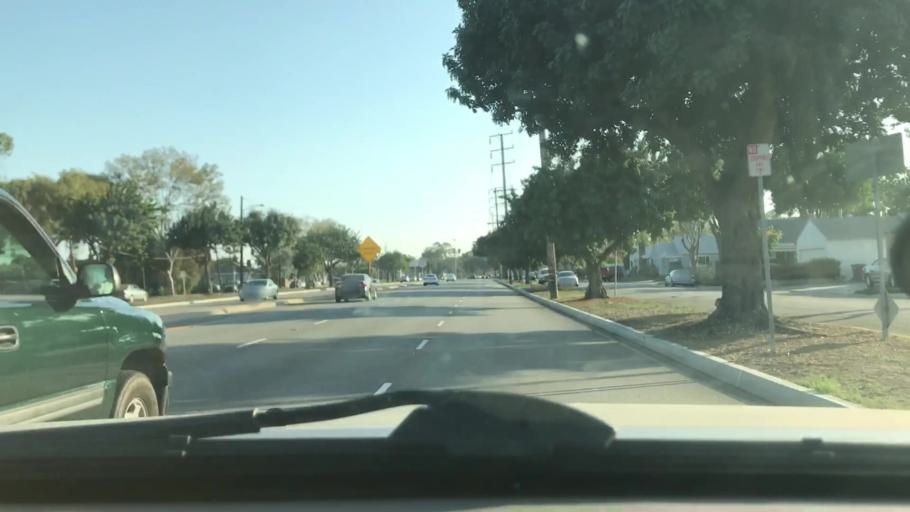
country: US
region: California
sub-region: Los Angeles County
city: Signal Hill
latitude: 33.7950
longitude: -118.1428
